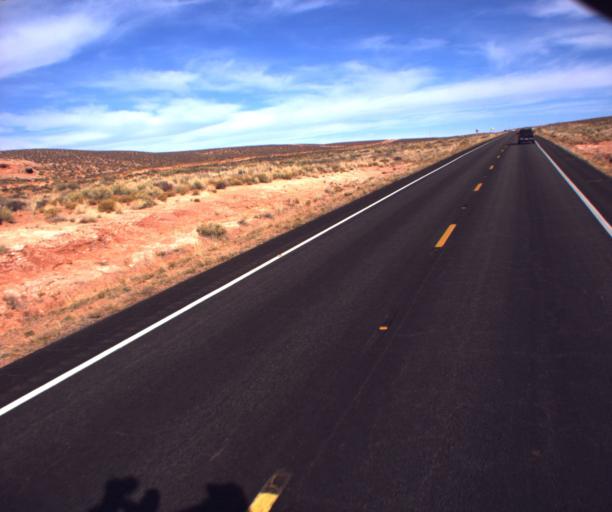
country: US
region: Arizona
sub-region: Apache County
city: Many Farms
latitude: 36.9249
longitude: -109.5958
